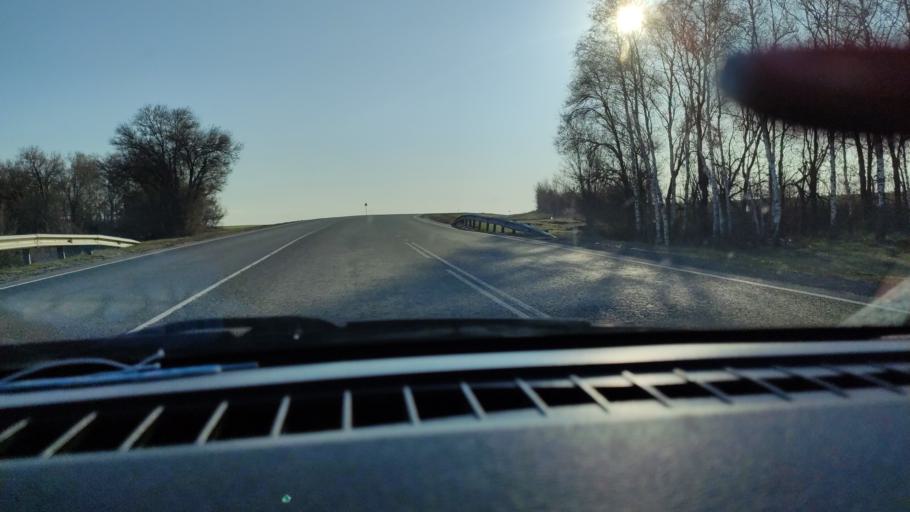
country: RU
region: Saratov
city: Balakovo
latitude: 52.1341
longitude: 47.7774
